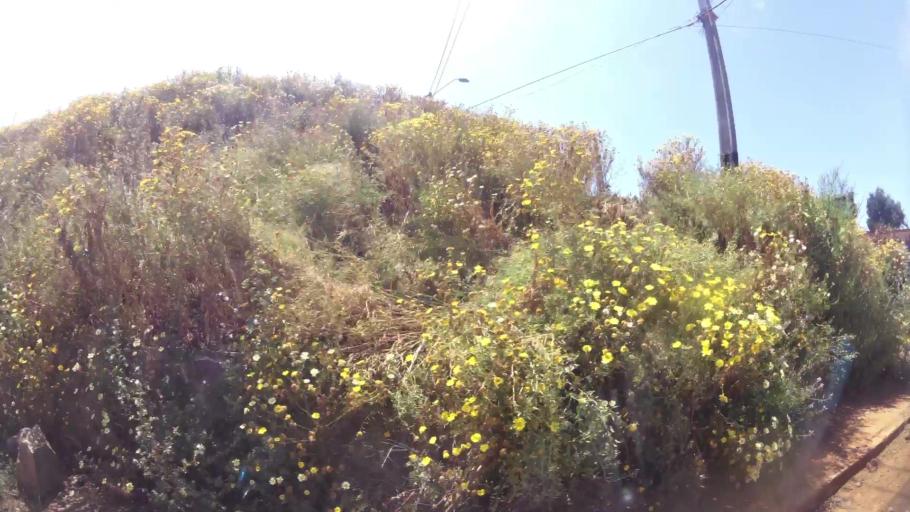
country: CL
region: Valparaiso
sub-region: Provincia de Valparaiso
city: Valparaiso
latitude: -33.0356
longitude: -71.6539
